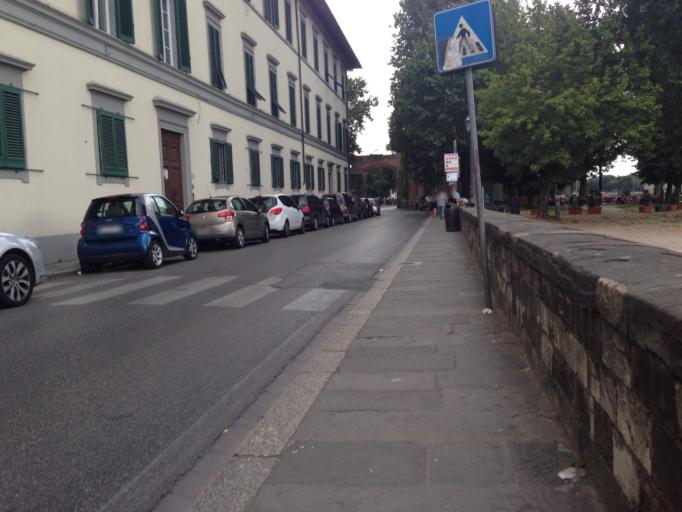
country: IT
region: Tuscany
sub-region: Province of Florence
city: Florence
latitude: 43.7715
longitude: 11.2418
